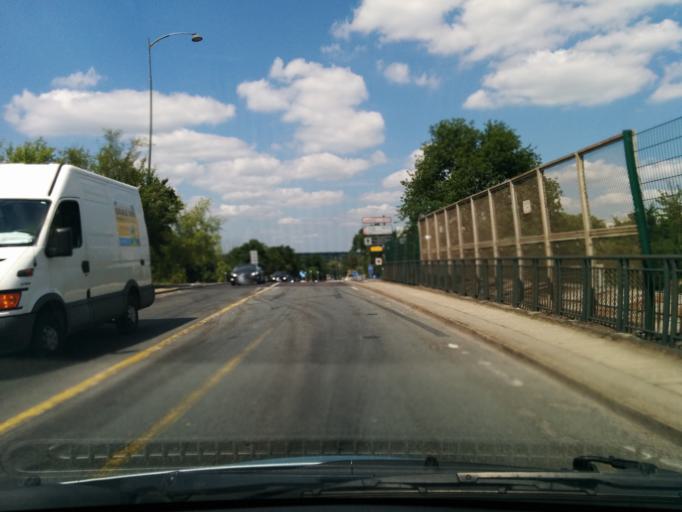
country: FR
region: Ile-de-France
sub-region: Departement des Yvelines
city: Buchelay
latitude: 48.9944
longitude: 1.6758
